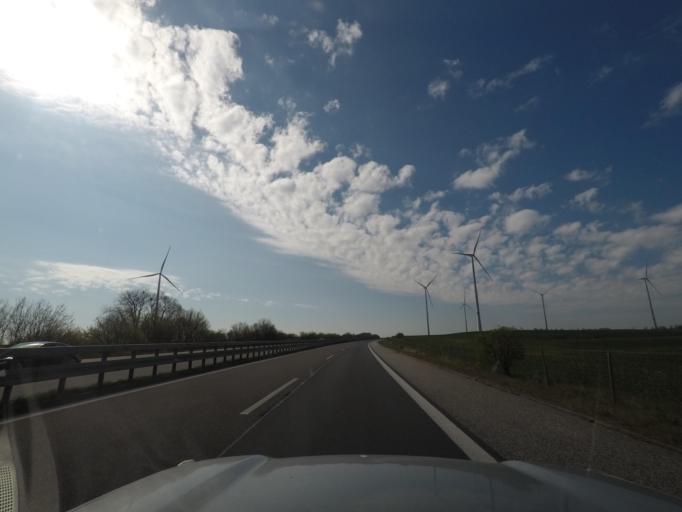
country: DE
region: Brandenburg
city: Grunow
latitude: 53.2836
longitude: 13.9900
